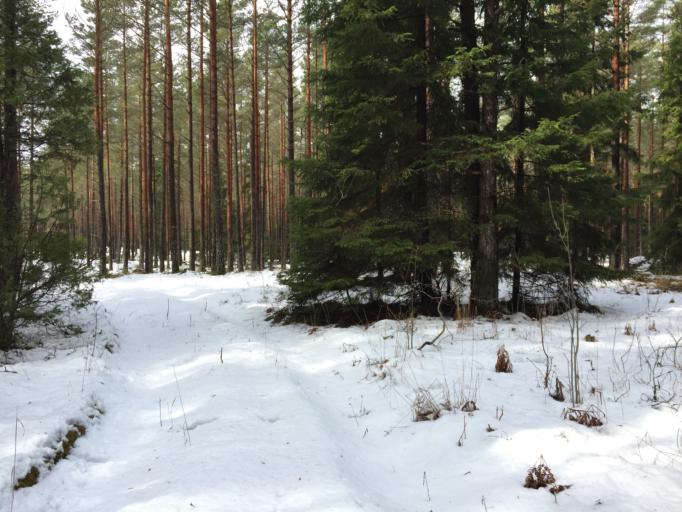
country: EE
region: Saare
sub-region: Kuressaare linn
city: Kuressaare
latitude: 58.3955
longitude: 22.1627
